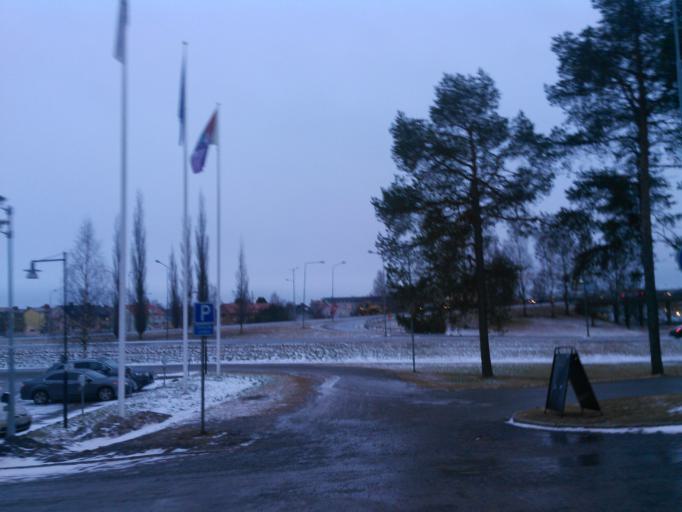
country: SE
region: Vaesterbotten
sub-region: Umea Kommun
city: Umea
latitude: 63.8336
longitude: 20.2615
